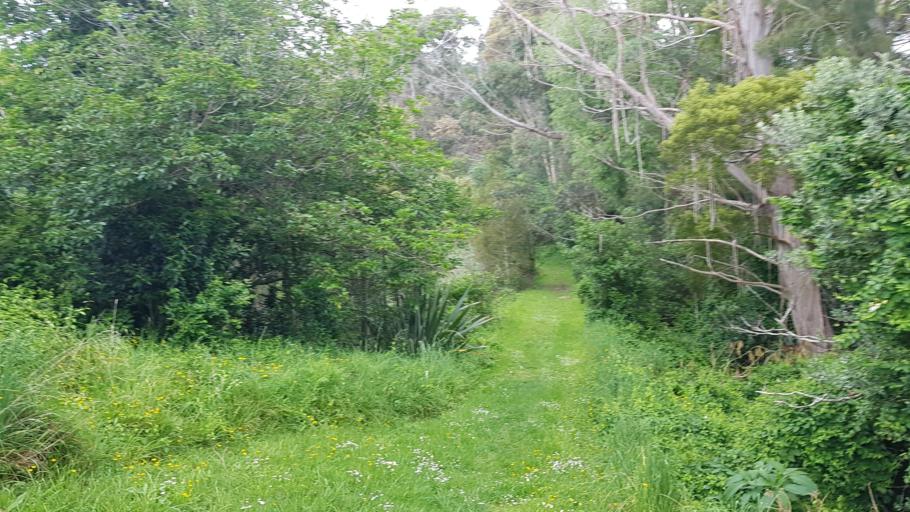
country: NZ
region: Auckland
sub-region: Auckland
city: Pakuranga
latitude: -36.7749
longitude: 175.0065
